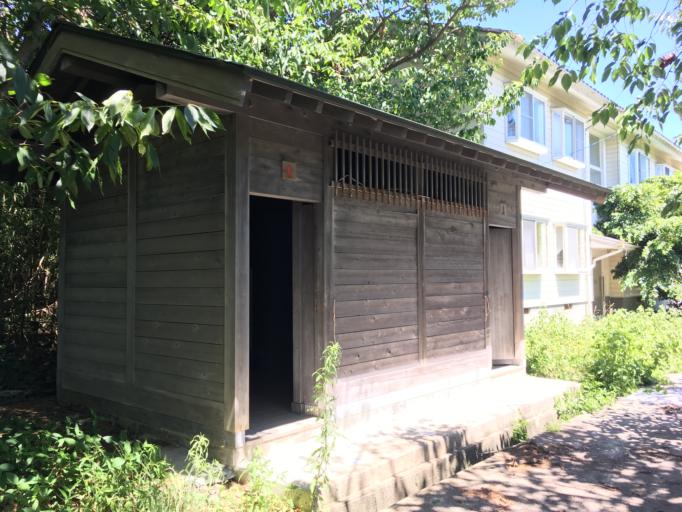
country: JP
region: Ishikawa
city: Nanao
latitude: 37.8500
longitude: 136.9178
